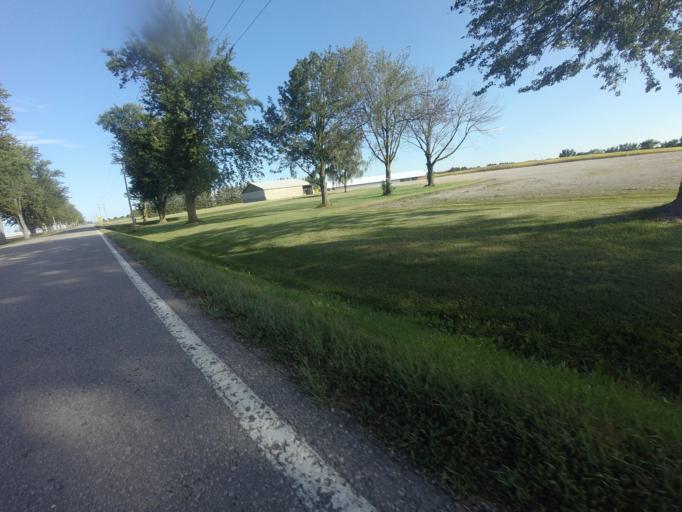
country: CA
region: Ontario
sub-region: Wellington County
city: Guelph
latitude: 43.6391
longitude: -80.3999
